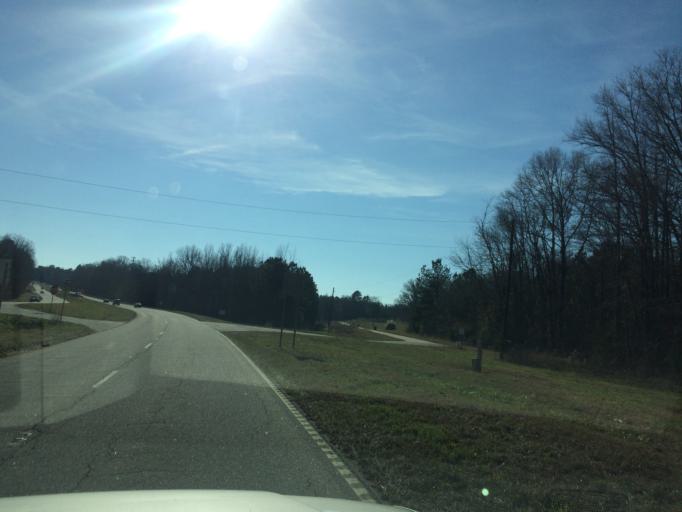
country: US
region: South Carolina
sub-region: Greenwood County
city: Greenwood
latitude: 34.2479
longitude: -82.0988
